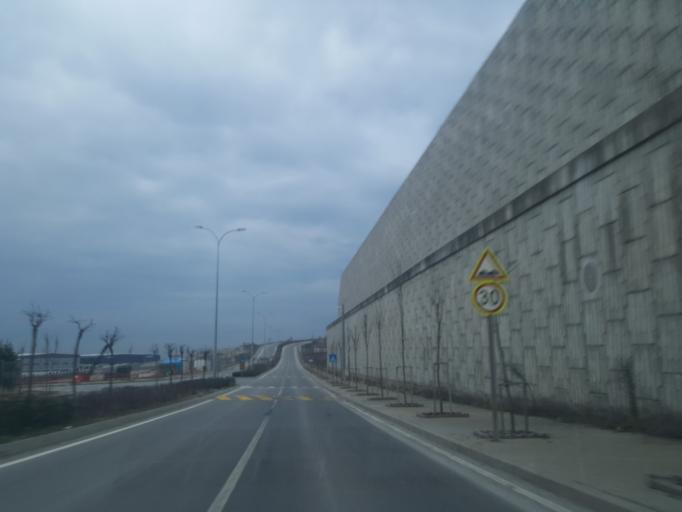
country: TR
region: Kocaeli
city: Tavsanli
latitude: 40.8325
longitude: 29.5545
